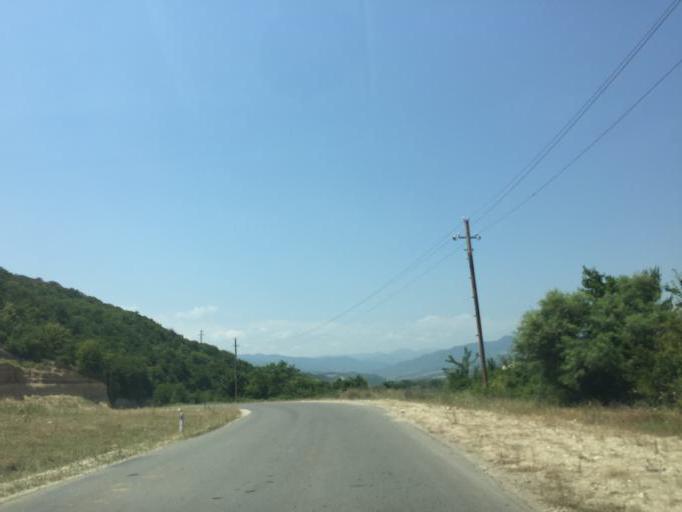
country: AZ
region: Tartar Rayon
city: Martakert
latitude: 40.1439
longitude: 46.5675
